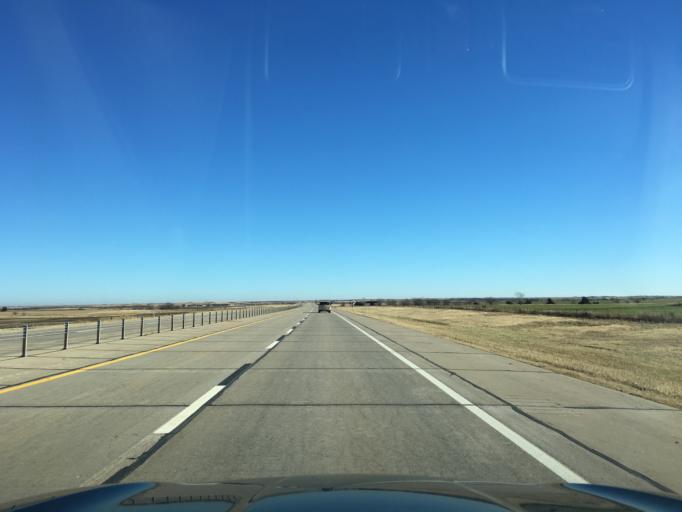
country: US
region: Oklahoma
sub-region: Noble County
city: Perry
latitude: 36.3990
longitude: -97.2939
